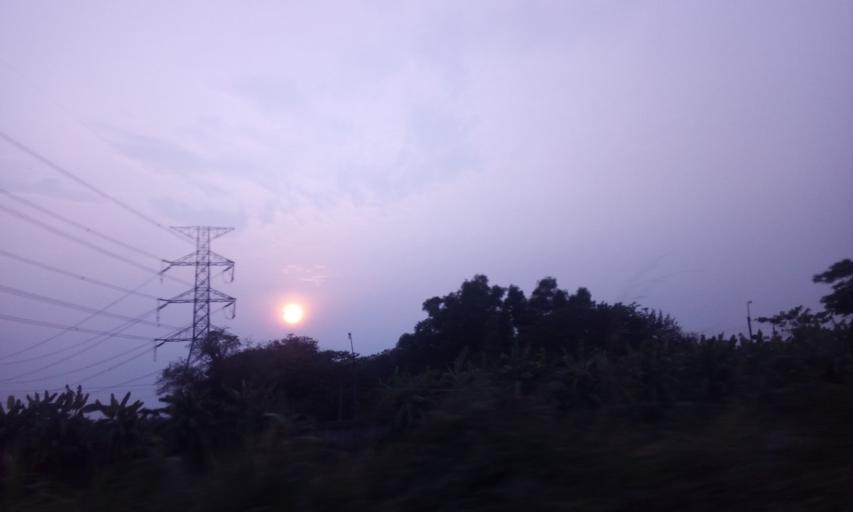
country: TH
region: Bangkok
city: Nong Chok
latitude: 13.9302
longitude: 100.8931
